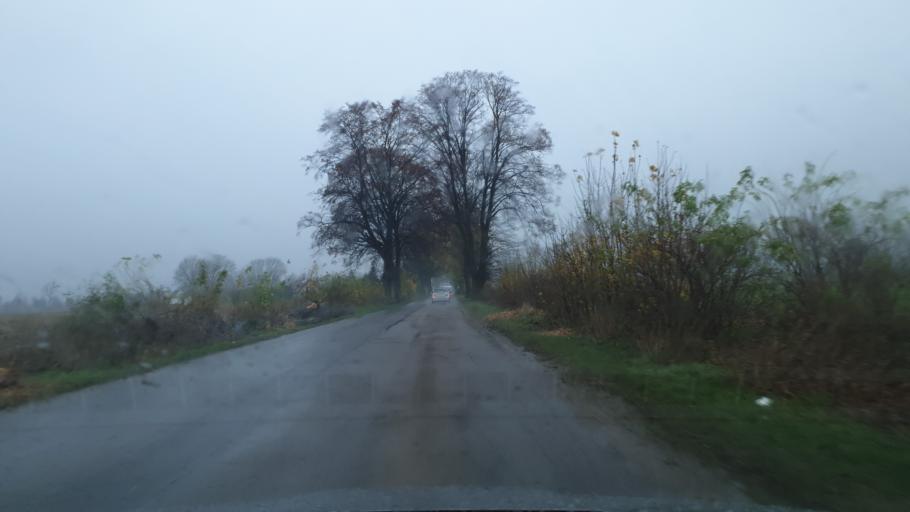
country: PL
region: Pomeranian Voivodeship
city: Strzelno
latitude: 54.7533
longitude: 18.2748
